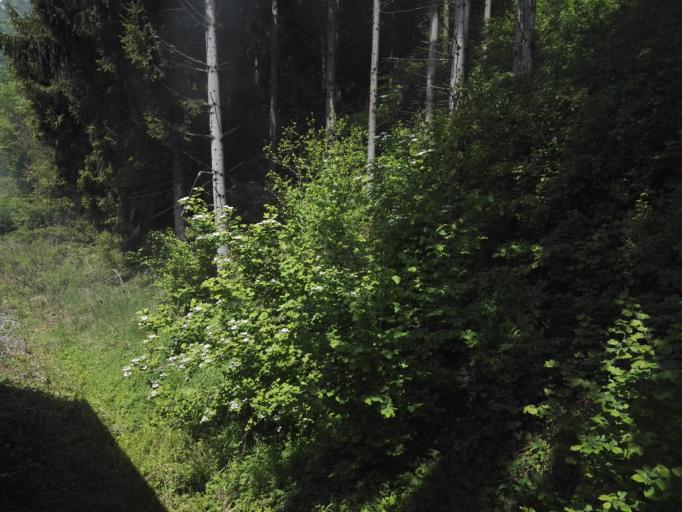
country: AT
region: Styria
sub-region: Politischer Bezirk Weiz
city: Anger
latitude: 47.2666
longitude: 15.7071
